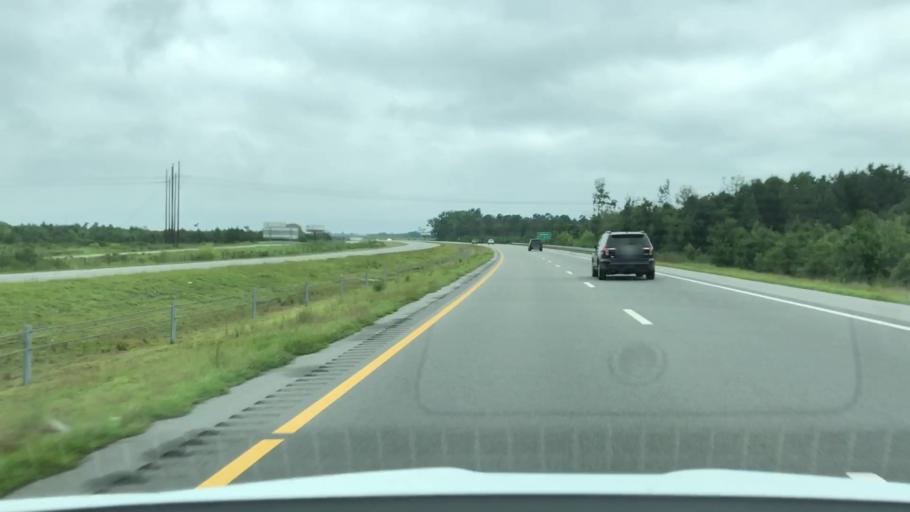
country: US
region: North Carolina
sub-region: Wayne County
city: Elroy
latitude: 35.3975
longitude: -77.8705
